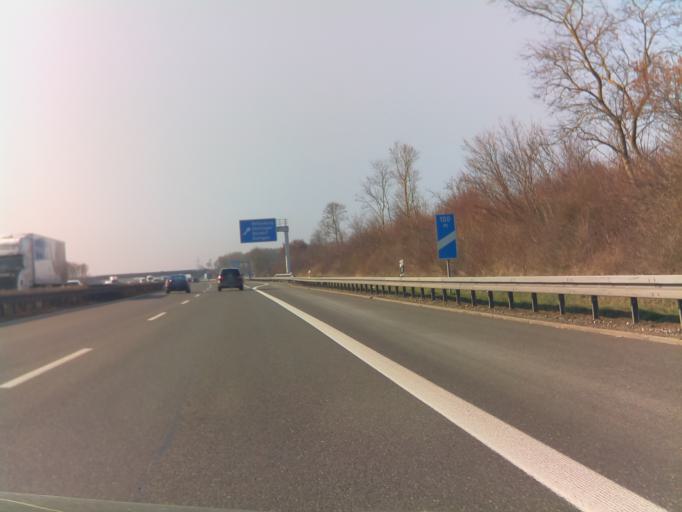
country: DE
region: Baden-Wuerttemberg
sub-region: Regierungsbezirk Stuttgart
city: Bondorf
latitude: 48.5080
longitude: 8.8501
